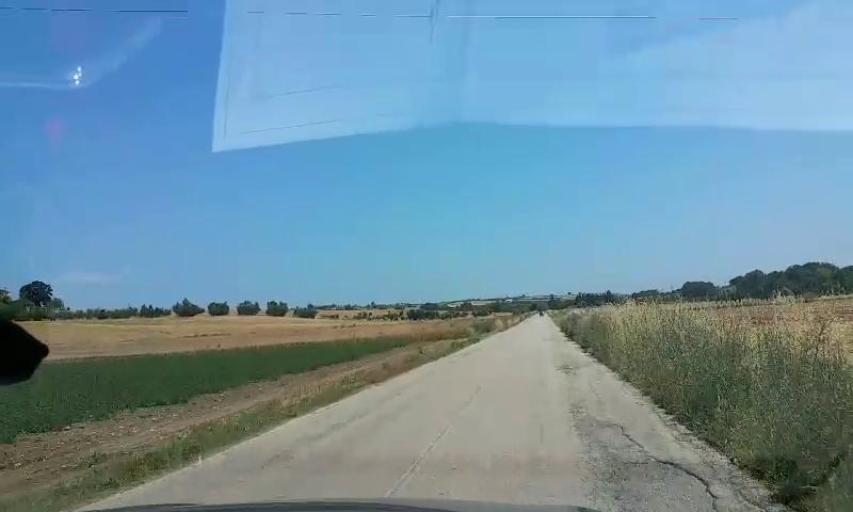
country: IT
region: Molise
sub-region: Provincia di Campobasso
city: San Giacomo degli Schiavoni
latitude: 41.9789
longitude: 14.9115
